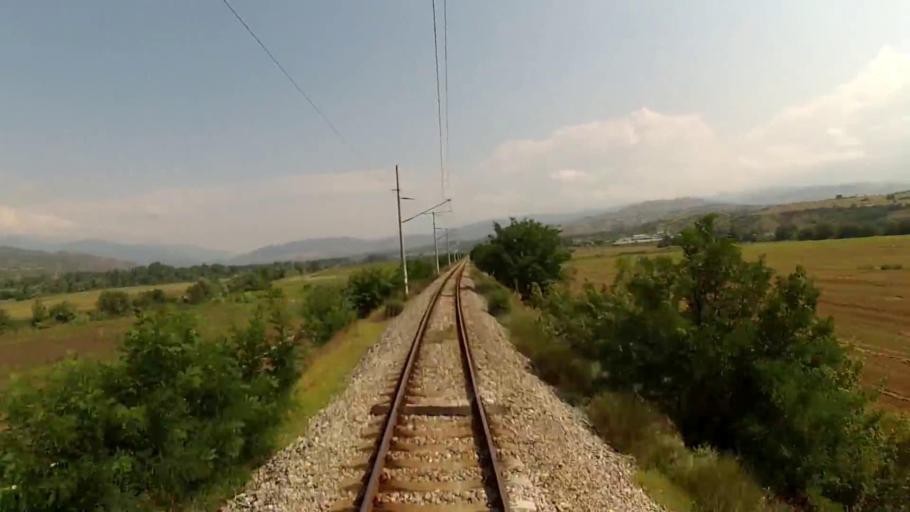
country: BG
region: Blagoevgrad
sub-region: Obshtina Strumyani
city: Strumyani
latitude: 41.6491
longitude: 23.1933
